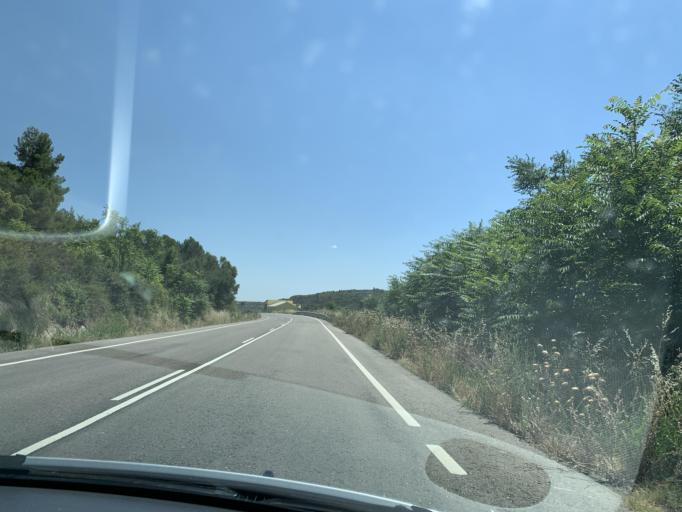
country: ES
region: Castille-La Mancha
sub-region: Provincia de Guadalajara
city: Zorita de los Canes
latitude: 40.3706
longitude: -2.9126
